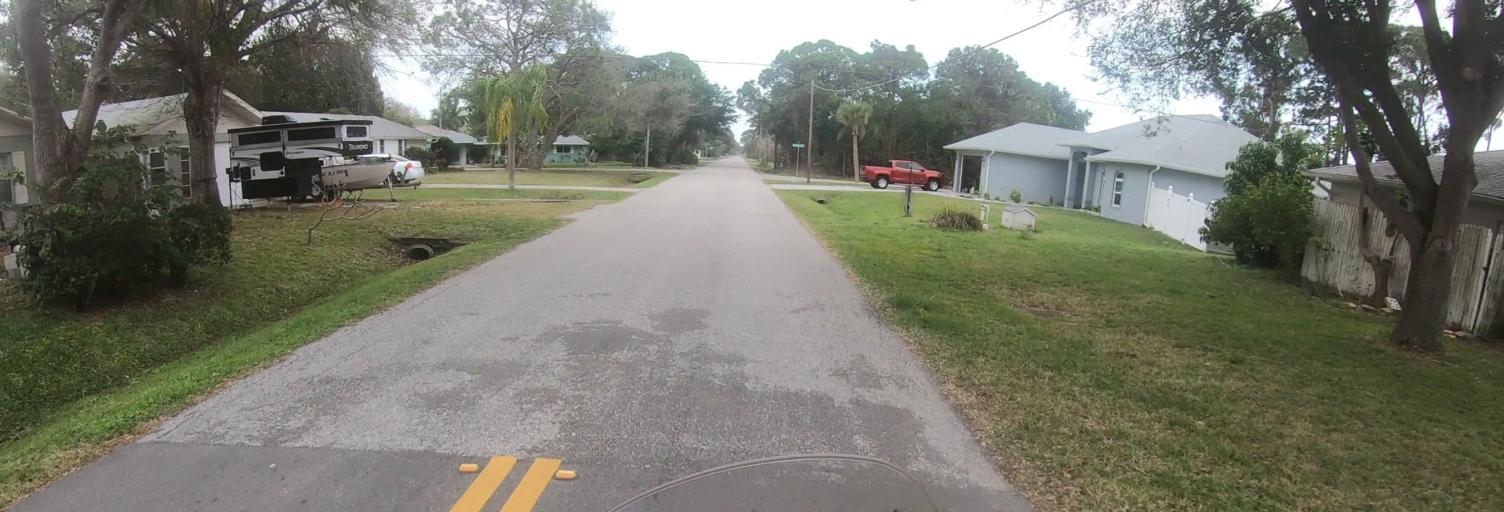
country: US
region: Florida
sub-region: Sarasota County
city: South Venice
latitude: 27.0563
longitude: -82.4297
